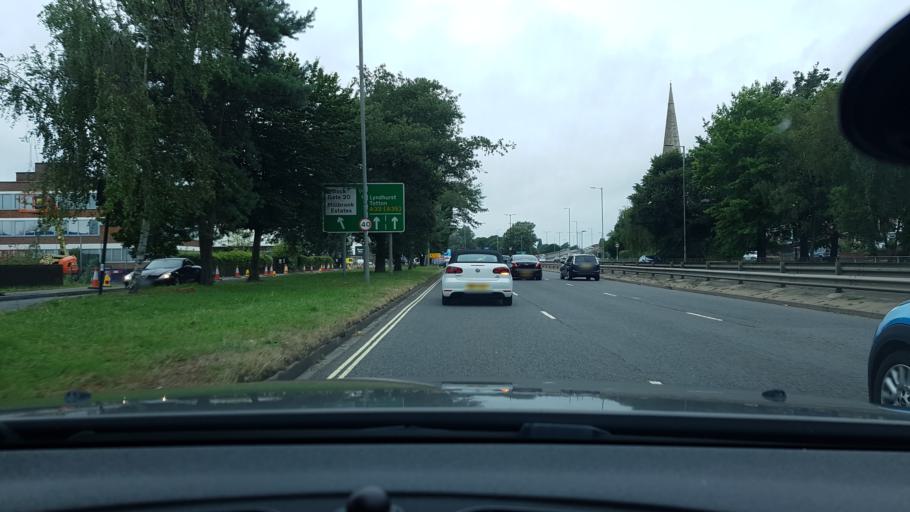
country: GB
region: England
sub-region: Hampshire
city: Marchwood
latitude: 50.9146
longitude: -1.4517
